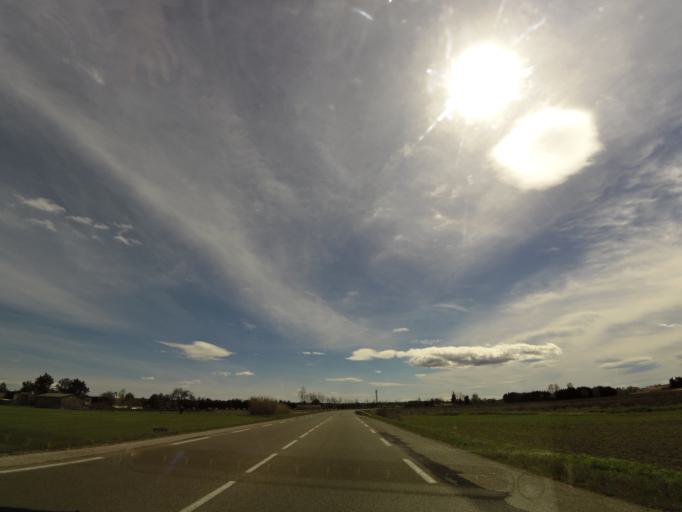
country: FR
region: Languedoc-Roussillon
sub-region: Departement du Gard
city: Bernis
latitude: 43.7620
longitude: 4.2796
